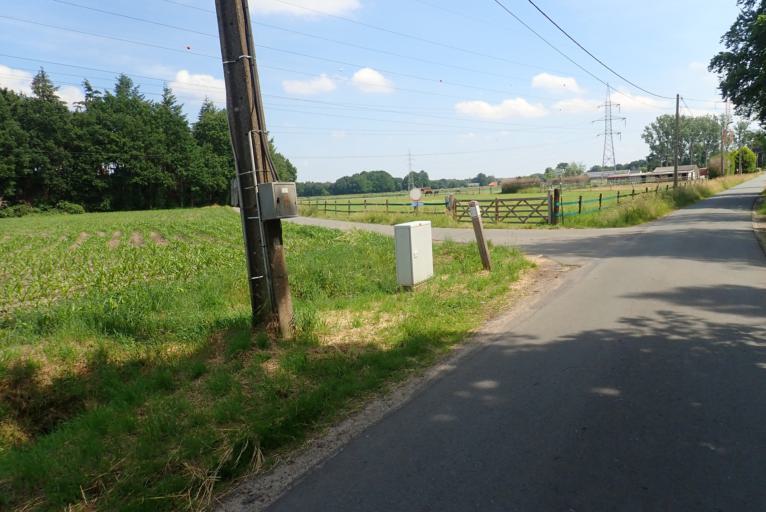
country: BE
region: Flanders
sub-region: Provincie Antwerpen
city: Zandhoven
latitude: 51.2284
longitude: 4.6935
